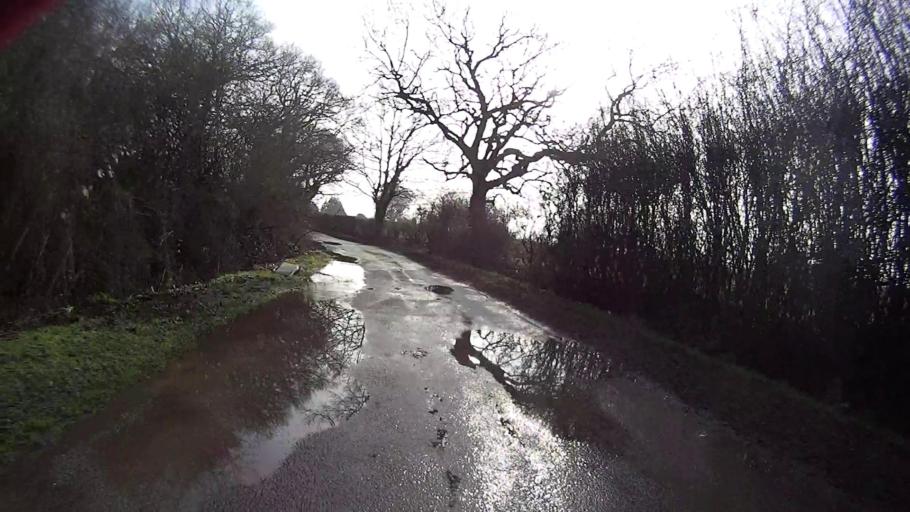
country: GB
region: England
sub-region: West Sussex
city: Copthorne
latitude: 51.1746
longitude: -0.1032
